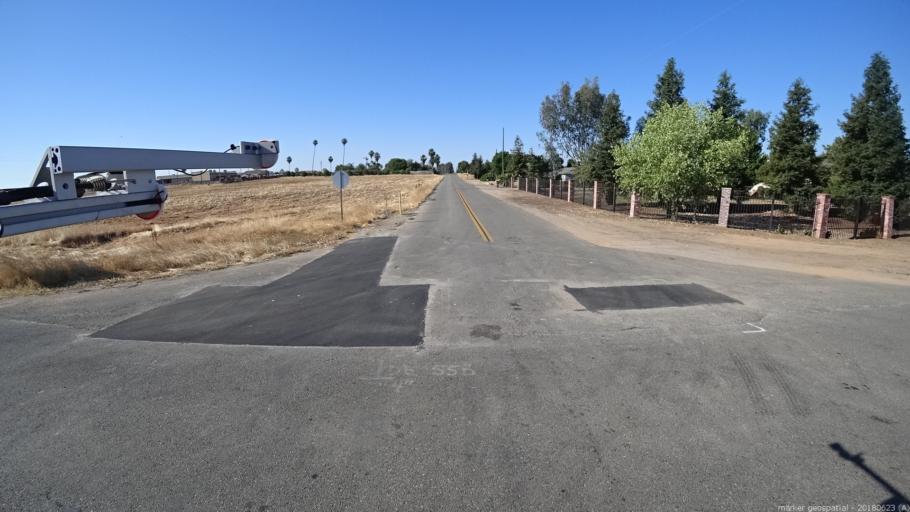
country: US
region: California
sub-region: Madera County
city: Bonadelle Ranchos-Madera Ranchos
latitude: 36.9595
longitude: -119.7961
